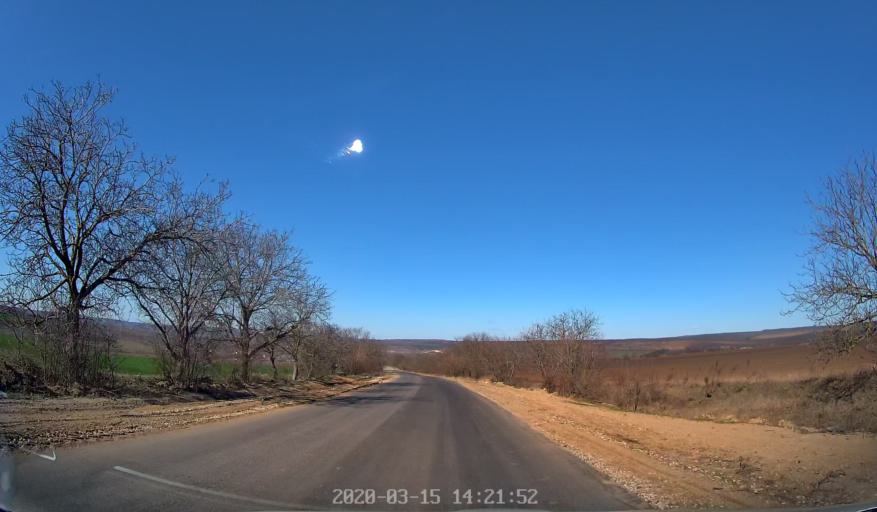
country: MD
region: Orhei
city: Orhei
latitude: 47.3227
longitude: 28.9257
